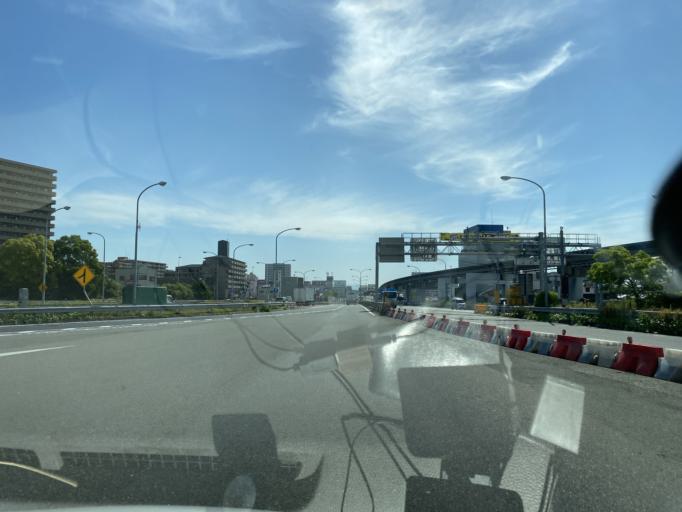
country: JP
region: Osaka
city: Ibaraki
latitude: 34.8081
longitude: 135.5466
